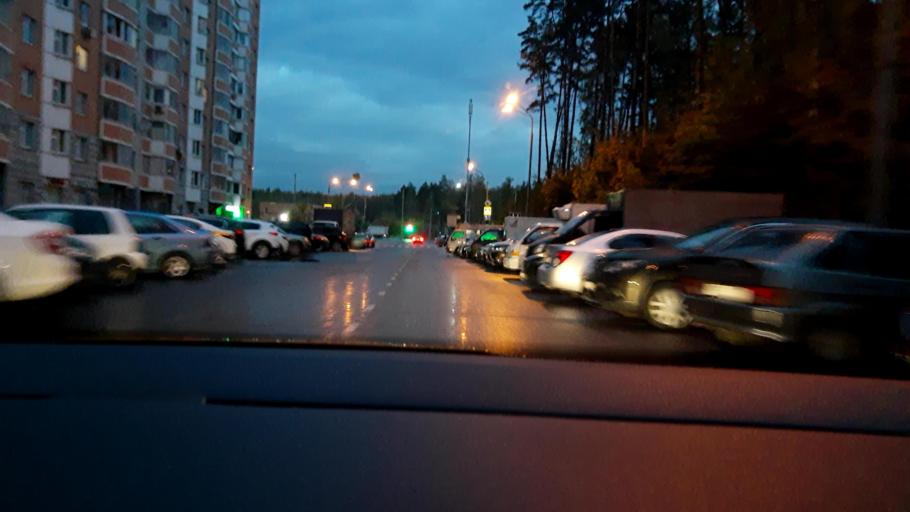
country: RU
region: Moscow
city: Vostochnyy
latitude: 55.8224
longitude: 37.8825
